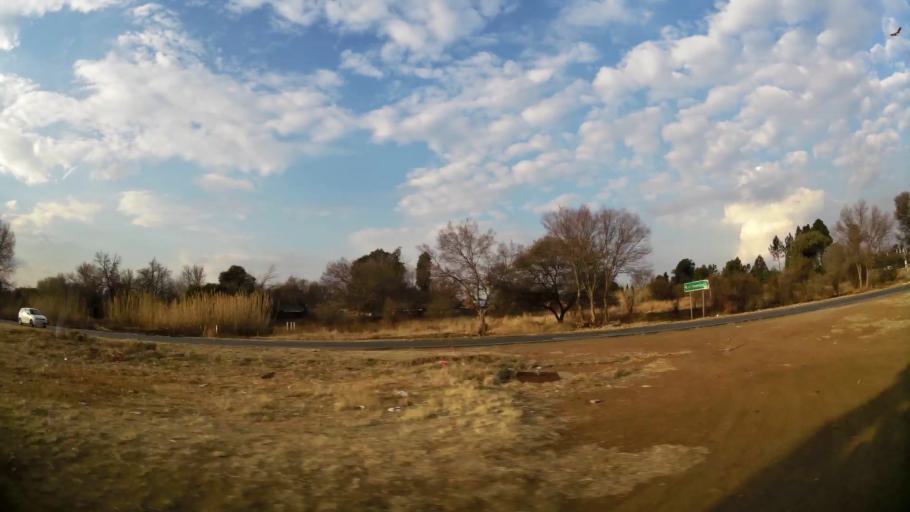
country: ZA
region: Gauteng
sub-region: Sedibeng District Municipality
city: Vanderbijlpark
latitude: -26.7082
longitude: 27.8147
